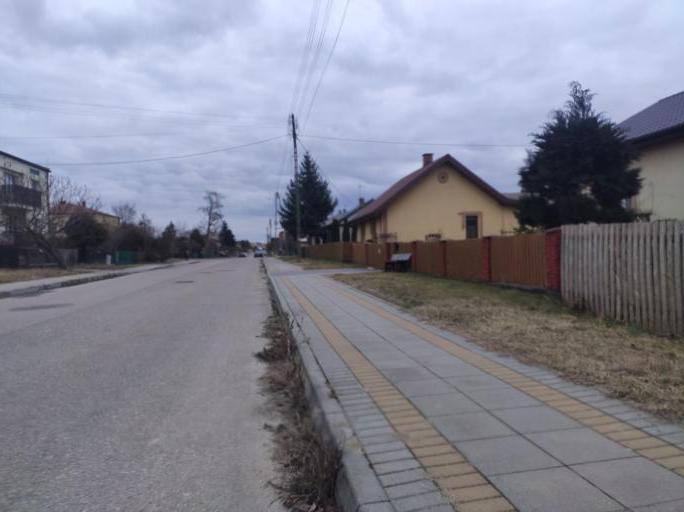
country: PL
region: Lublin Voivodeship
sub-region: Powiat lubartowski
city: Kock
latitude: 51.6393
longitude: 22.4381
